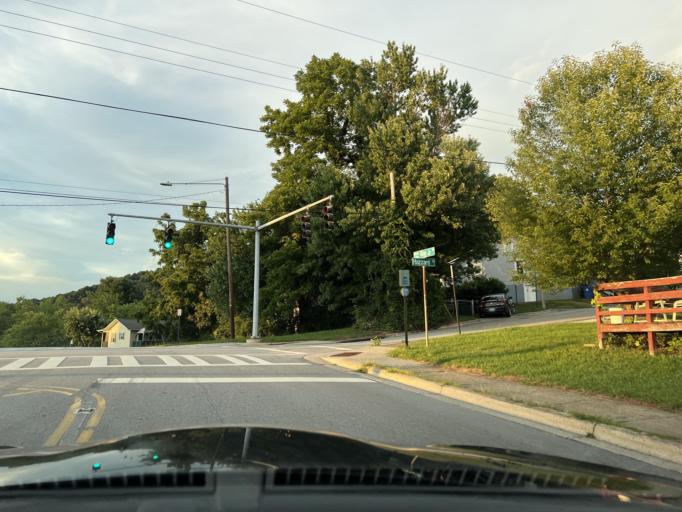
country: US
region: North Carolina
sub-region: Buncombe County
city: Asheville
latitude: 35.5935
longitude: -82.5437
